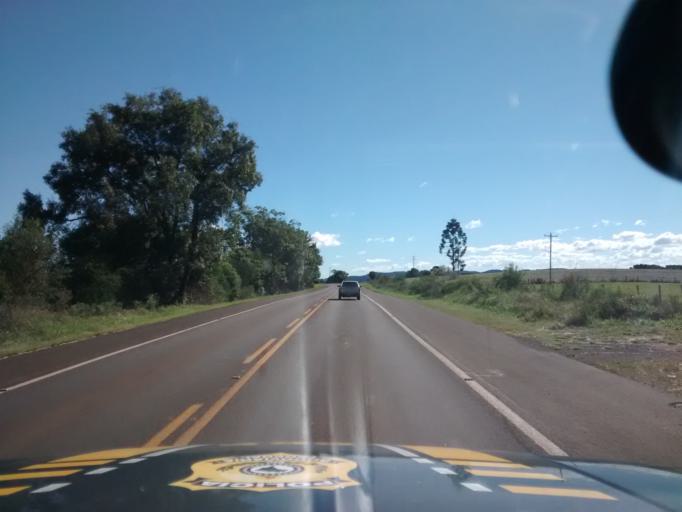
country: BR
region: Rio Grande do Sul
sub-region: Vacaria
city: Vacaria
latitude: -28.3549
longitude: -51.1245
